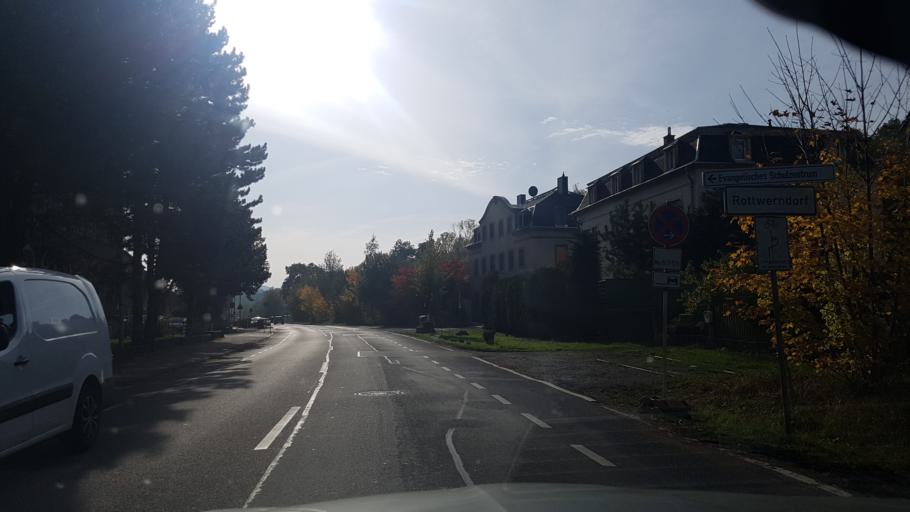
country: DE
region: Saxony
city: Pirna
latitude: 50.9390
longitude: 13.9447
